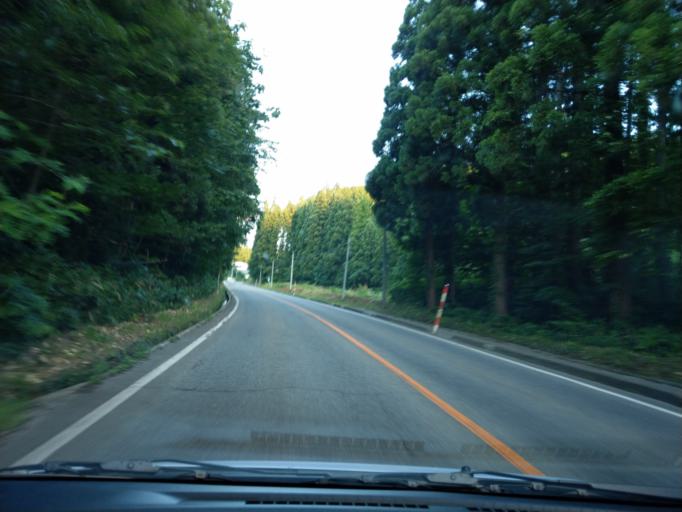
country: JP
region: Akita
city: Kakunodatemachi
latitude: 39.6033
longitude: 140.5715
